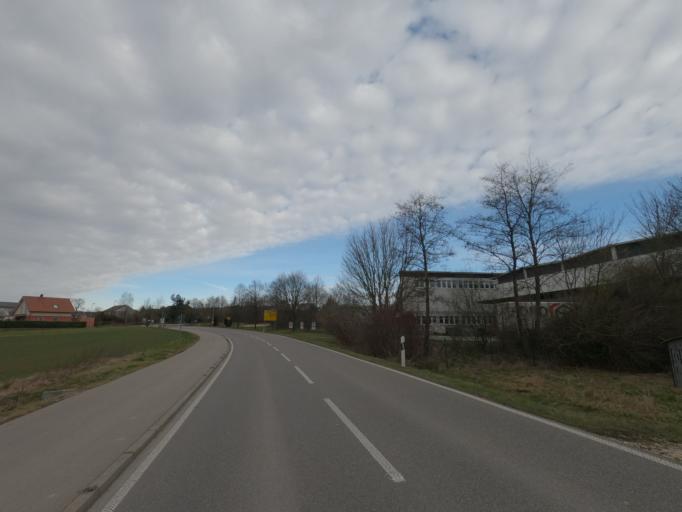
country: DE
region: Baden-Wuerttemberg
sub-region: Regierungsbezirk Stuttgart
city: Schlierbach
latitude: 48.6702
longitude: 9.5295
